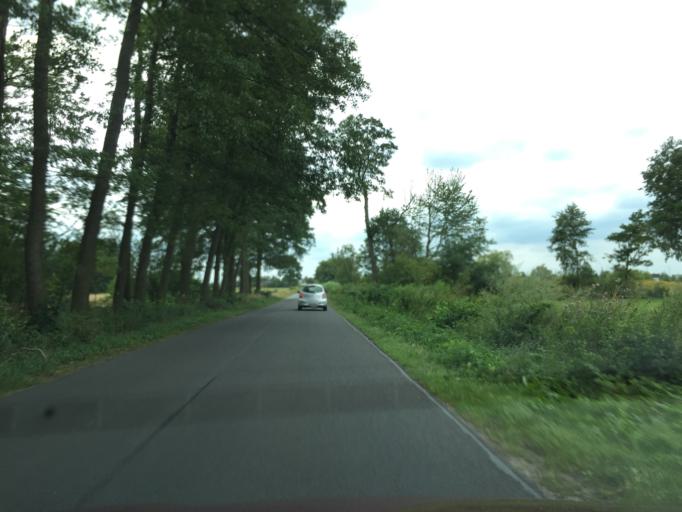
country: PL
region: Greater Poland Voivodeship
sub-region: Powiat kaliski
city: Stawiszyn
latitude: 51.9482
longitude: 18.1724
